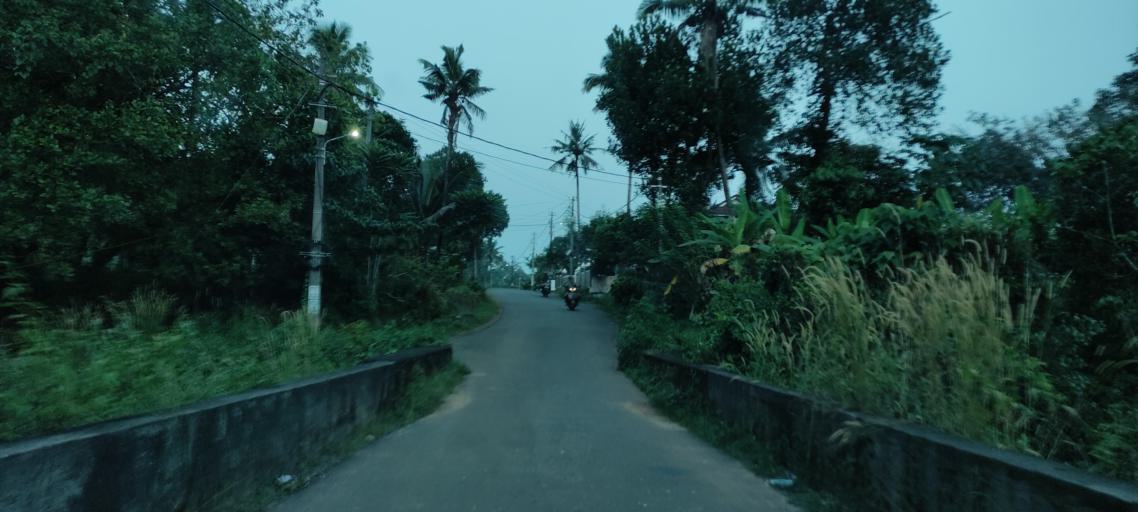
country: IN
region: Kerala
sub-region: Pattanamtitta
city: Adur
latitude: 9.1596
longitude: 76.7563
